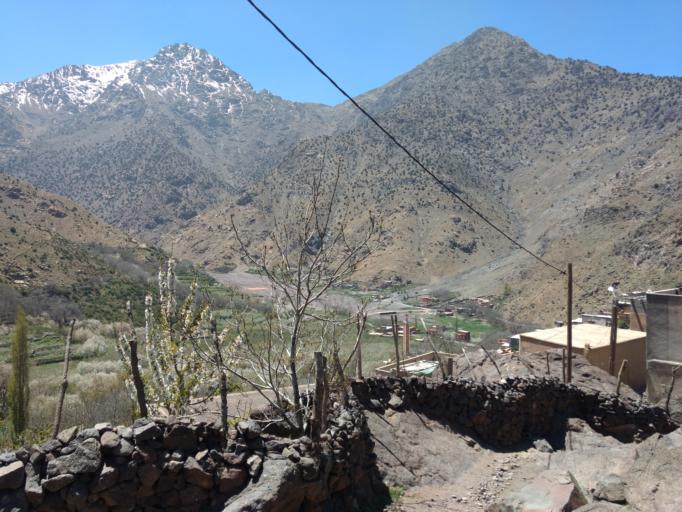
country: MA
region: Marrakech-Tensift-Al Haouz
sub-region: Al-Haouz
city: Moulay Brahim
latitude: 31.1263
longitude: -7.9140
